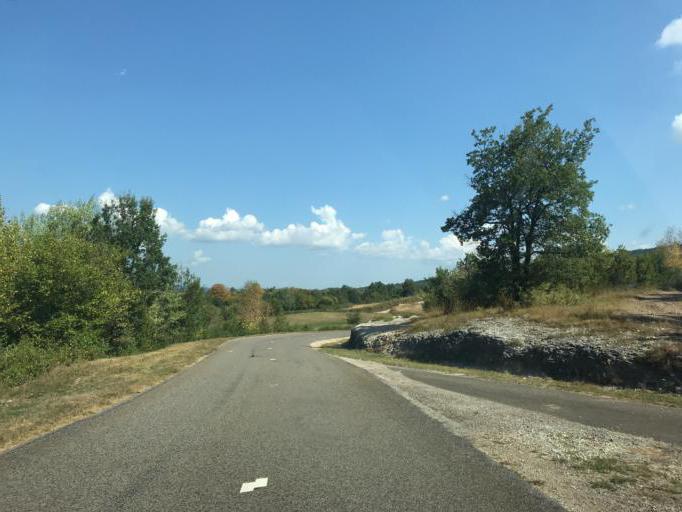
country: FR
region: Franche-Comte
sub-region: Departement du Jura
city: Moirans-en-Montagne
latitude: 46.4626
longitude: 5.7256
